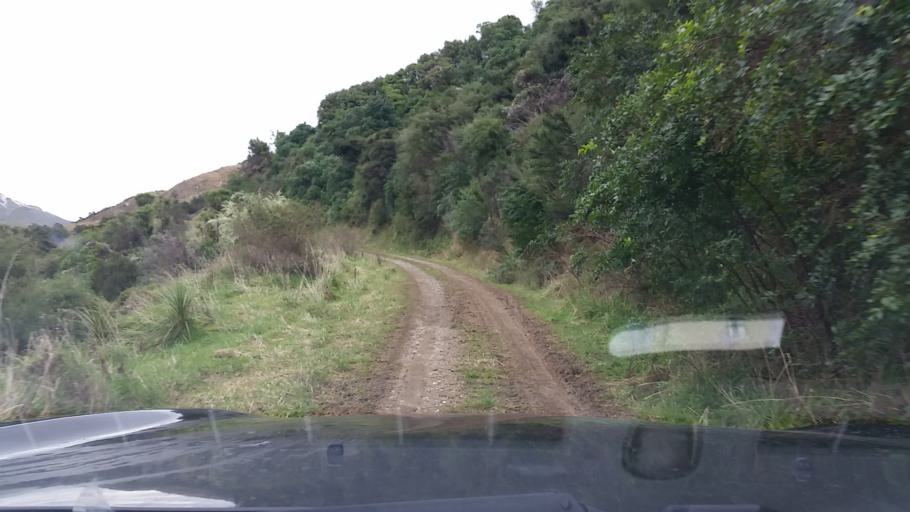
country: NZ
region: Marlborough
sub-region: Marlborough District
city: Blenheim
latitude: -41.8830
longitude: 174.0771
